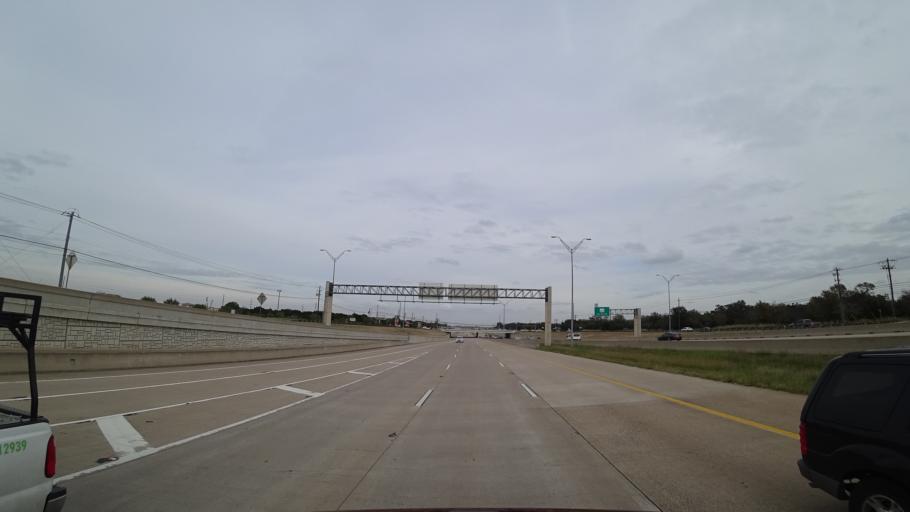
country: US
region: Texas
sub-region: Williamson County
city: Jollyville
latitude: 30.4753
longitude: -97.7682
